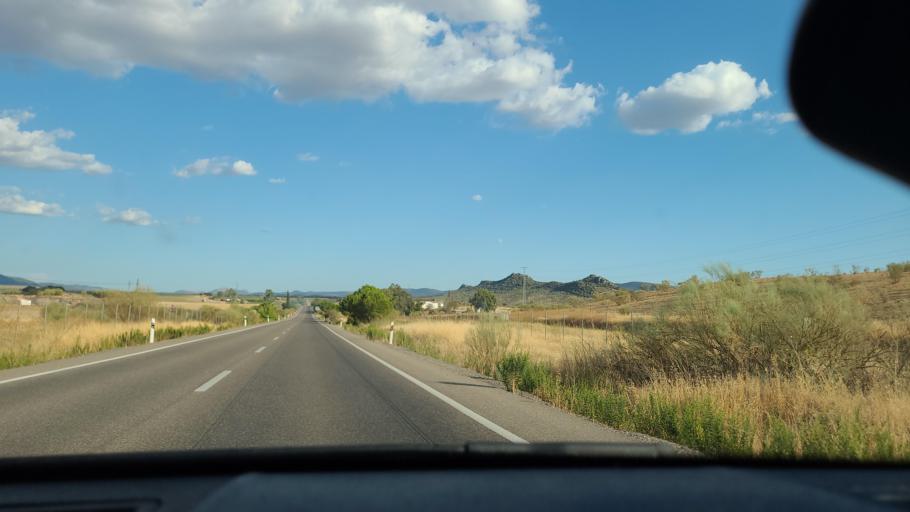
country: ES
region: Andalusia
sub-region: Province of Cordoba
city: Belmez
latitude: 38.2724
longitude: -5.1940
